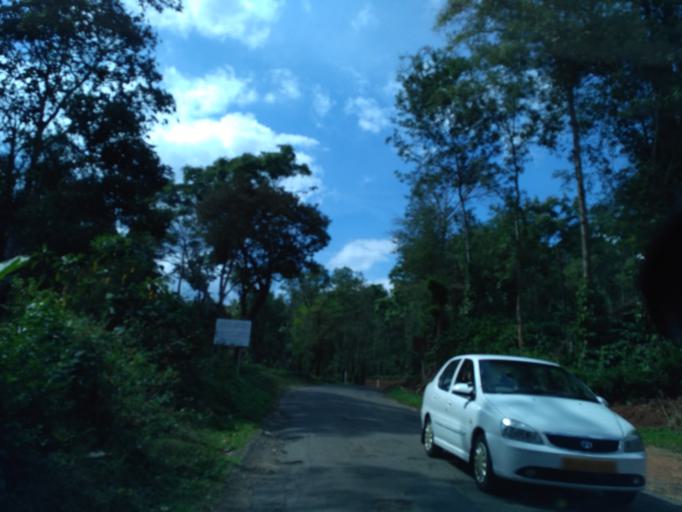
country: IN
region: Karnataka
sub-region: Kodagu
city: Madikeri
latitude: 12.3548
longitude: 75.6762
